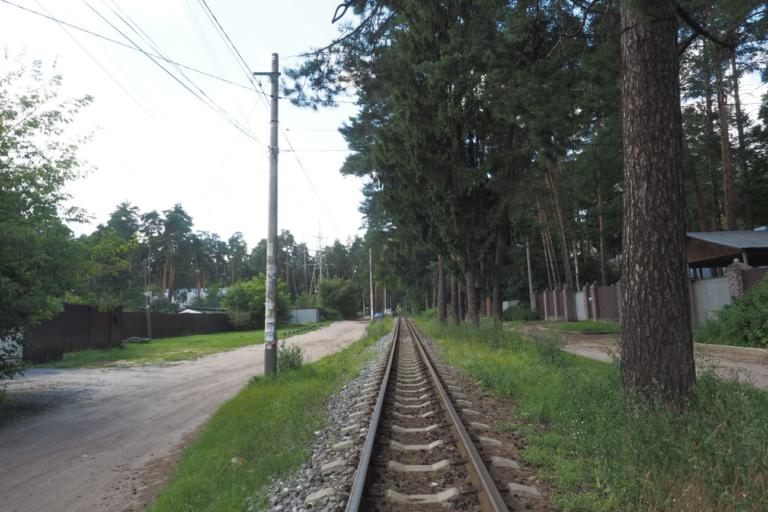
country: RU
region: Moskovskaya
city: Kratovo
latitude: 55.5852
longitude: 38.1566
